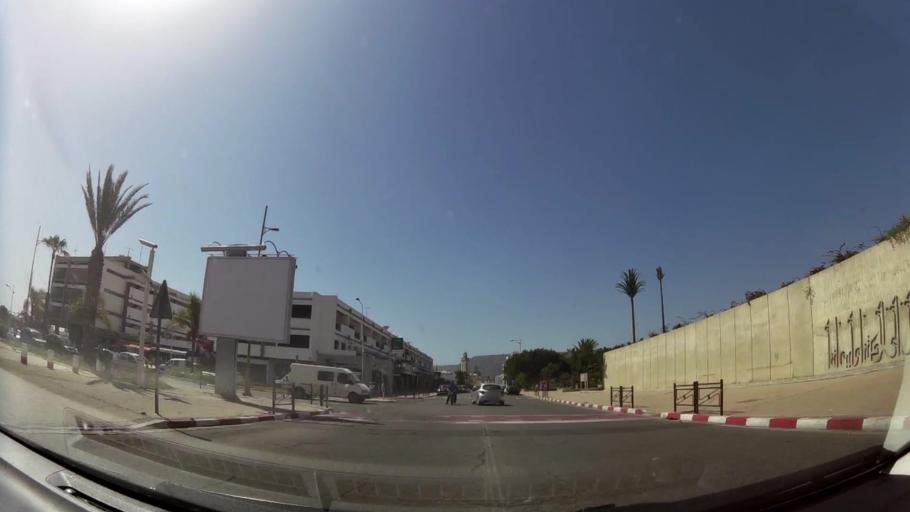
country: MA
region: Souss-Massa-Draa
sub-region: Agadir-Ida-ou-Tnan
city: Agadir
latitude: 30.4210
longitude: -9.5975
